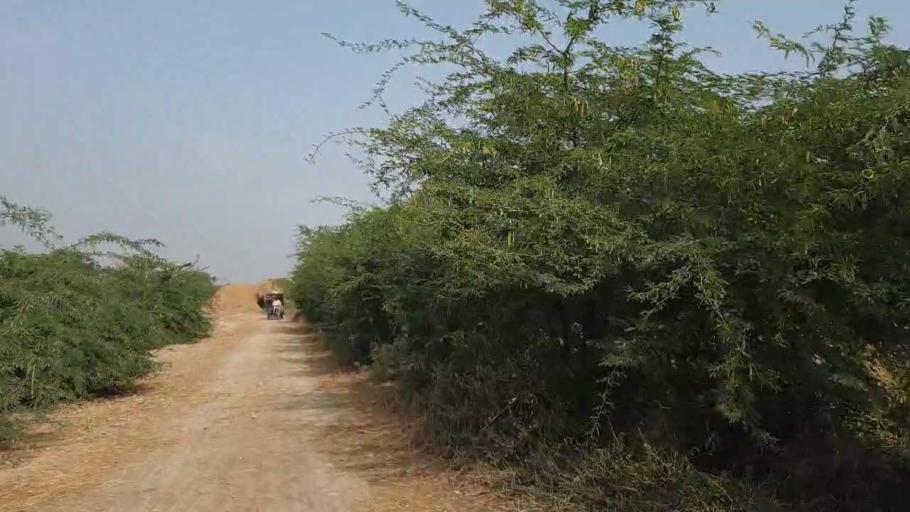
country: PK
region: Sindh
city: Kario
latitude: 24.7582
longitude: 68.5478
